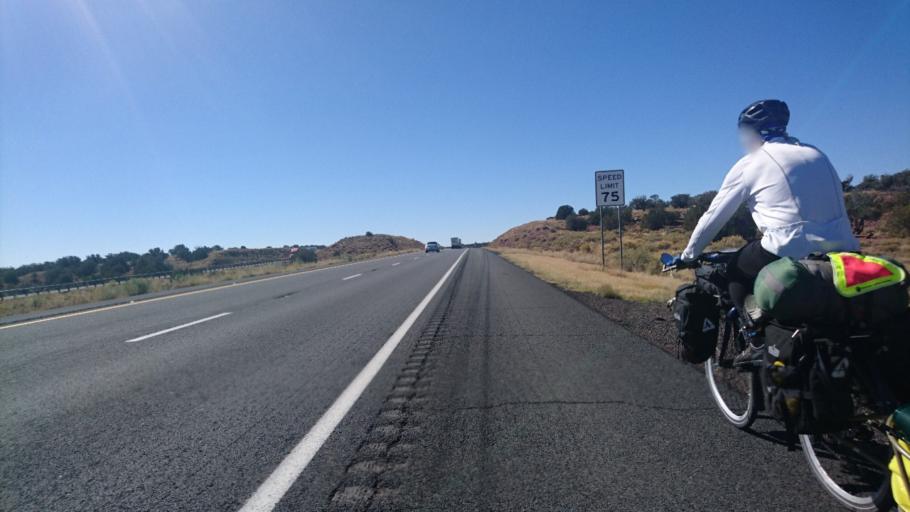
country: US
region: Arizona
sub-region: Apache County
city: Houck
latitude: 35.2792
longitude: -109.2505
